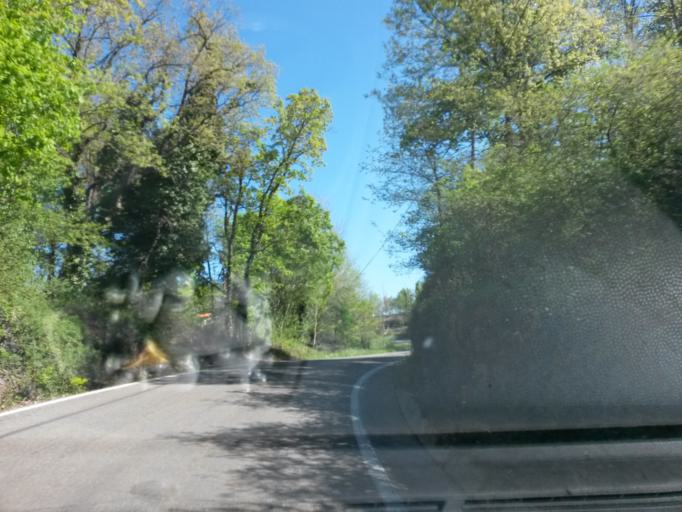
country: ES
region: Catalonia
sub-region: Provincia de Girona
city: Sant Cristofol de les Fonts
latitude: 42.1763
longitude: 2.5036
